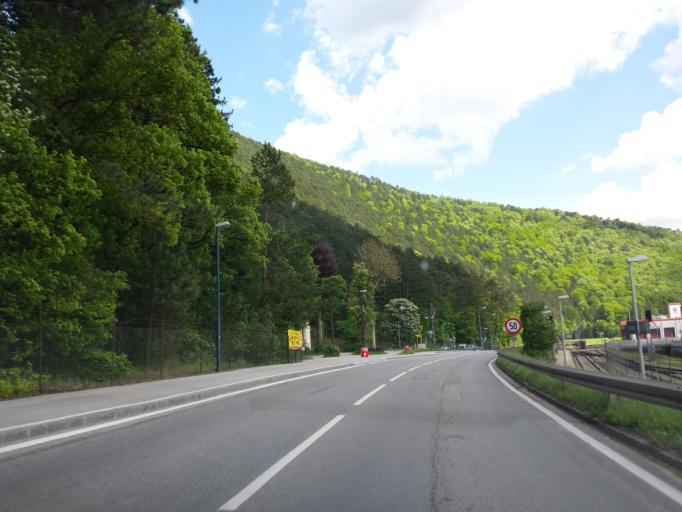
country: AT
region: Lower Austria
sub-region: Politischer Bezirk Wiener Neustadt
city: Pernitz
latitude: 47.8940
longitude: 15.9781
